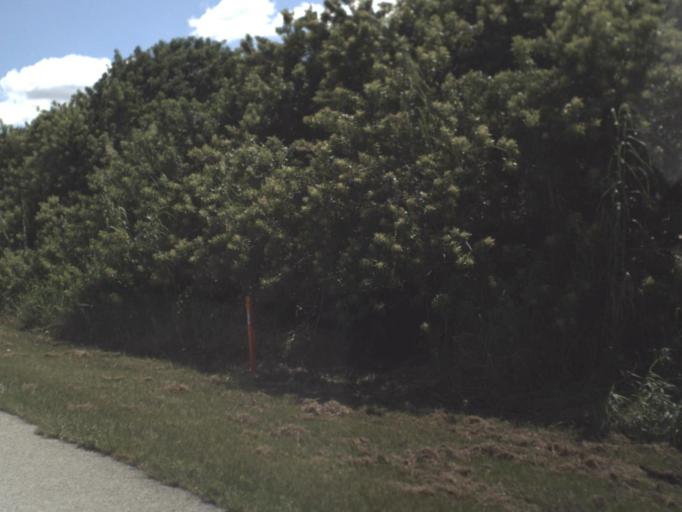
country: US
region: Florida
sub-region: Collier County
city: Lely Resort
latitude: 26.0102
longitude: -81.6162
